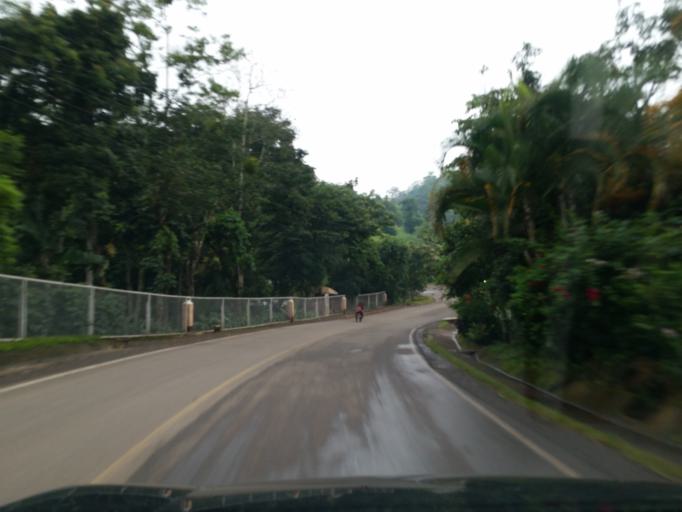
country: NI
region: Matagalpa
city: San Ramon
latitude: 13.1275
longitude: -85.7394
